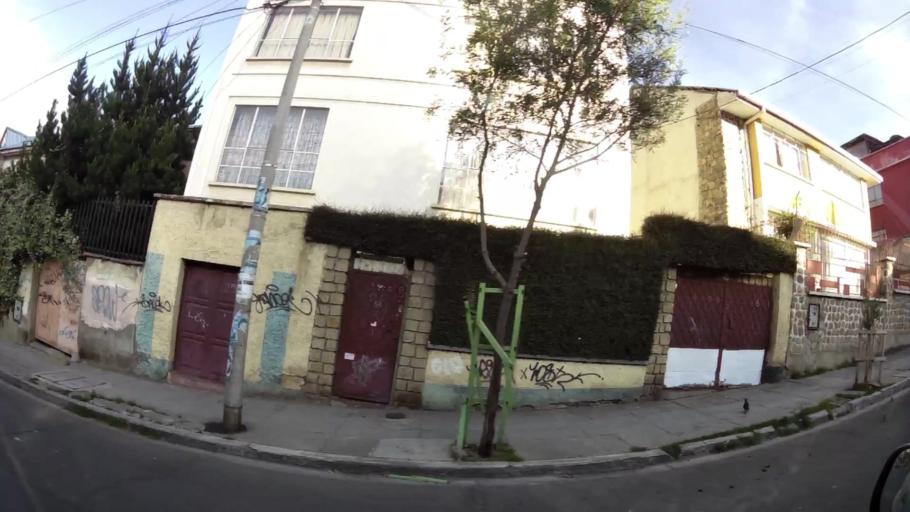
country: BO
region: La Paz
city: La Paz
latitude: -16.4924
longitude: -68.1232
